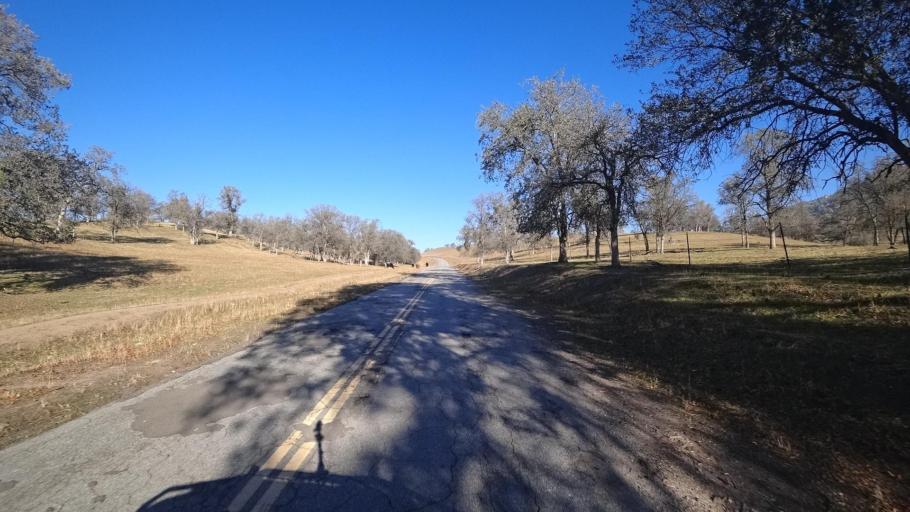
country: US
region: California
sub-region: Kern County
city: Alta Sierra
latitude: 35.7561
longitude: -118.8186
